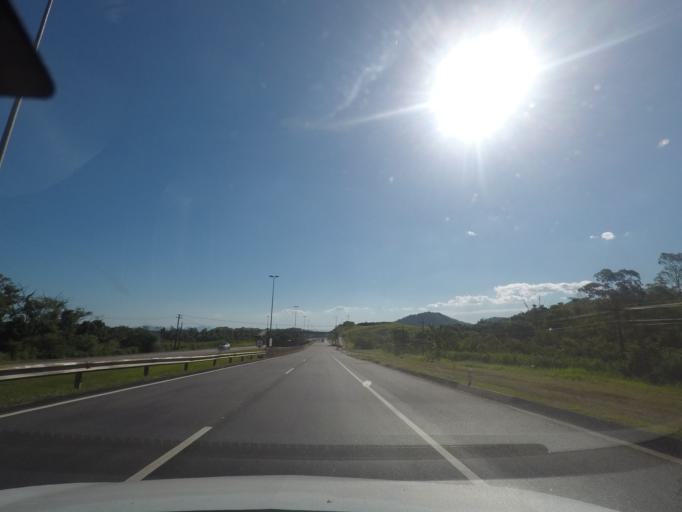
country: BR
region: Rio de Janeiro
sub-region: Guapimirim
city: Guapimirim
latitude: -22.6446
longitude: -43.0683
